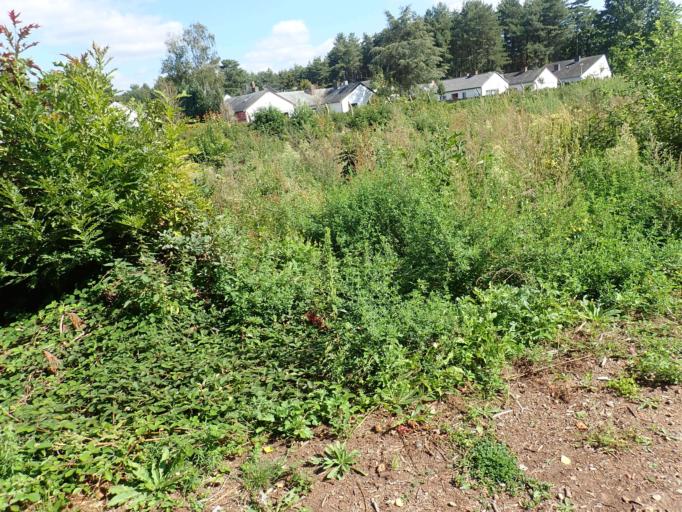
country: BE
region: Flanders
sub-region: Provincie Antwerpen
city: Westerlo
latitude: 51.1264
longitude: 4.8980
